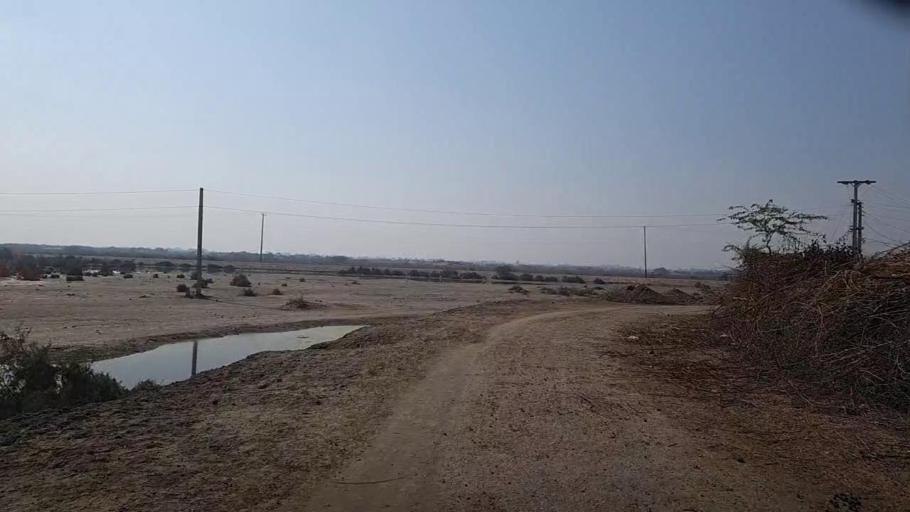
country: PK
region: Sindh
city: Bozdar
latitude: 27.2545
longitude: 68.5953
